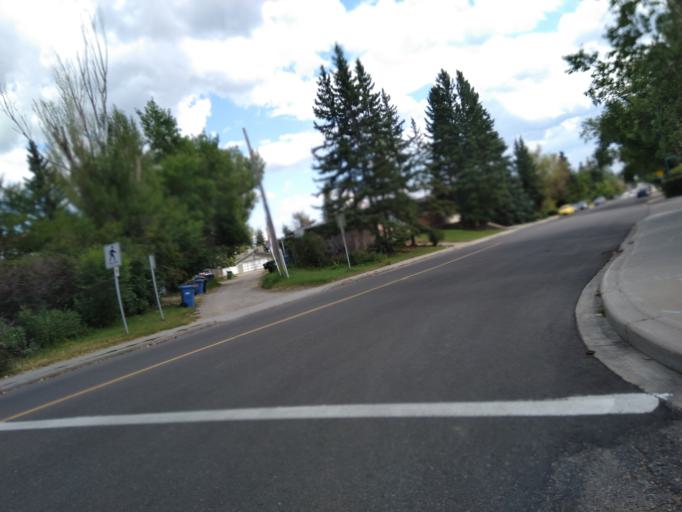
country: CA
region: Alberta
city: Calgary
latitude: 51.0815
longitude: -114.1200
